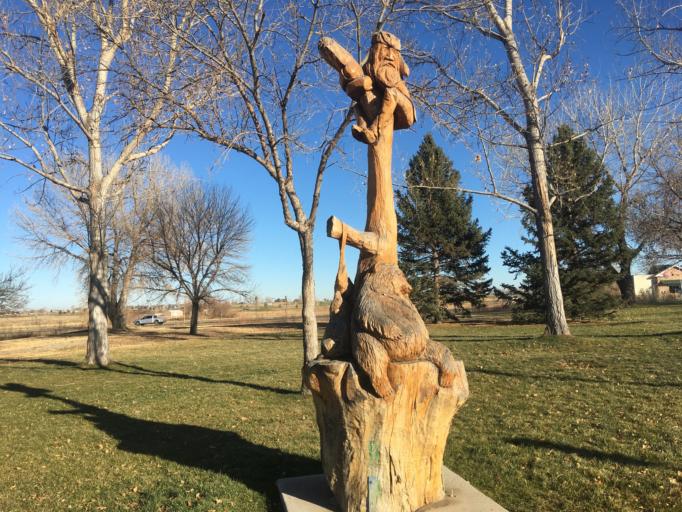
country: US
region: Colorado
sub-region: Weld County
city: Firestone
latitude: 40.1228
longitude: -104.9432
